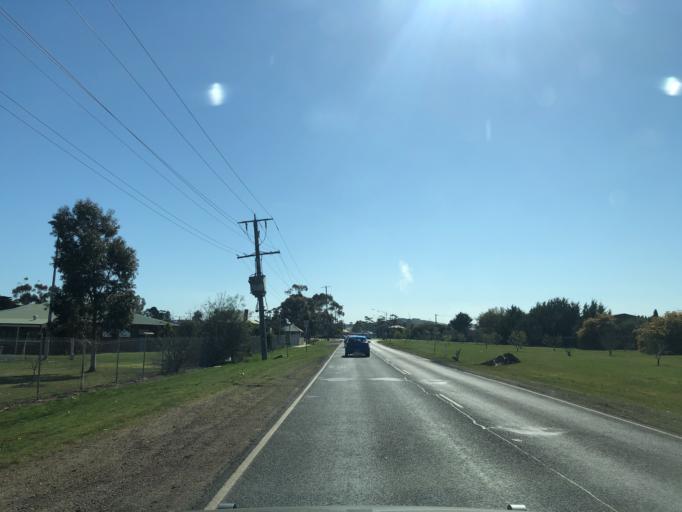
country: AU
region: Victoria
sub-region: Hume
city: Diggers Rest
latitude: -37.6298
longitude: 144.7224
